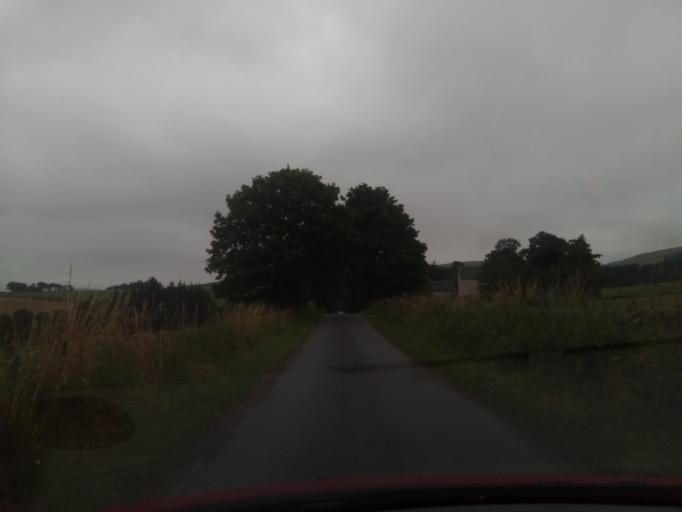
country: GB
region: Scotland
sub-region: The Scottish Borders
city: Galashiels
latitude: 55.6688
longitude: -2.8807
